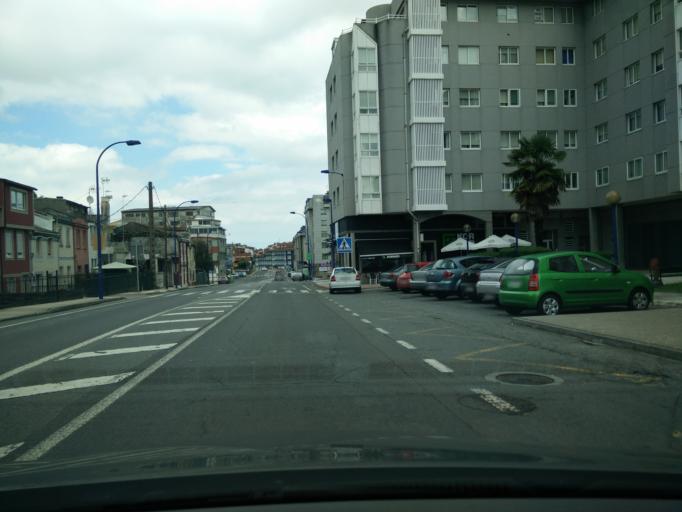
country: ES
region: Galicia
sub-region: Provincia da Coruna
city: Culleredo
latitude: 43.3206
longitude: -8.3841
